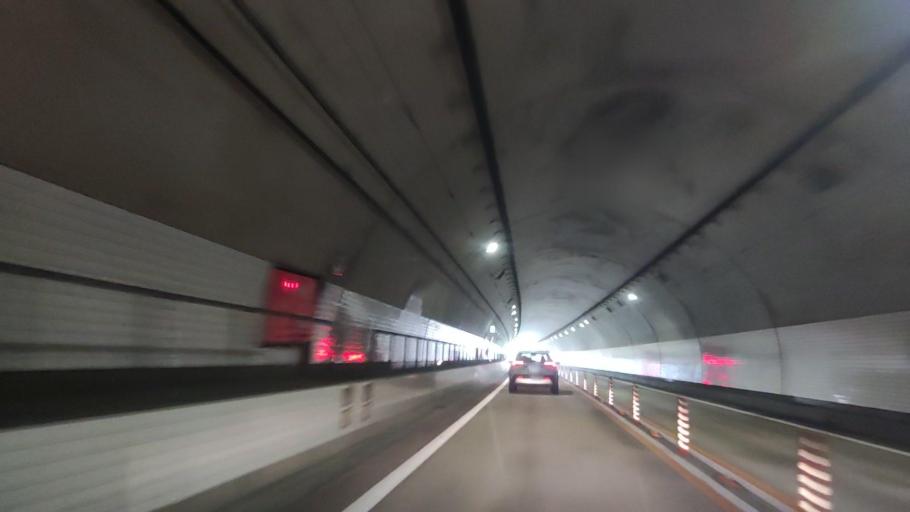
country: JP
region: Kyoto
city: Miyazu
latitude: 35.5541
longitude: 135.1306
